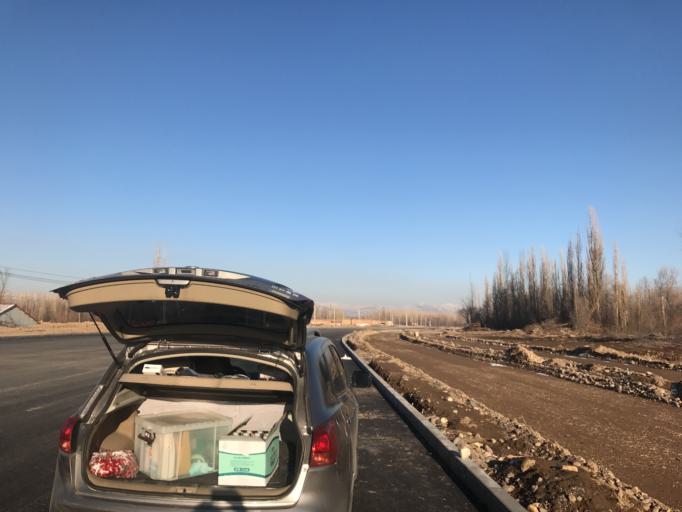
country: CN
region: Xinjiang Uygur Zizhiqu
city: Dadamtu
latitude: 43.9730
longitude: 81.2613
